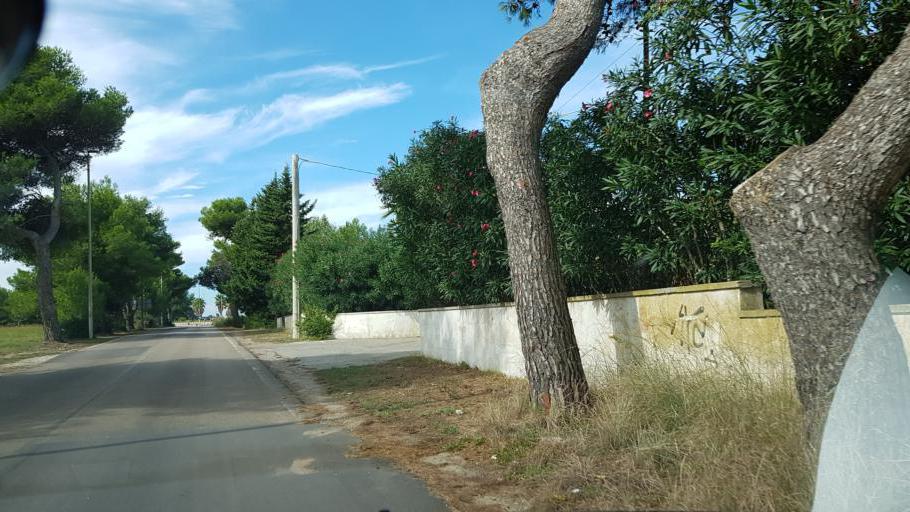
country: IT
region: Apulia
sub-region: Provincia di Lecce
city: Borgagne
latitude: 40.2544
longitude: 18.4409
